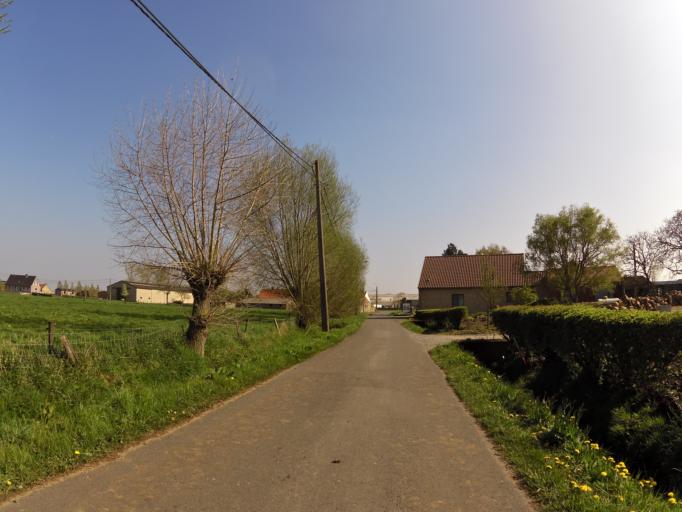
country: BE
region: Flanders
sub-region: Provincie West-Vlaanderen
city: Koekelare
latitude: 51.1163
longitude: 2.9899
